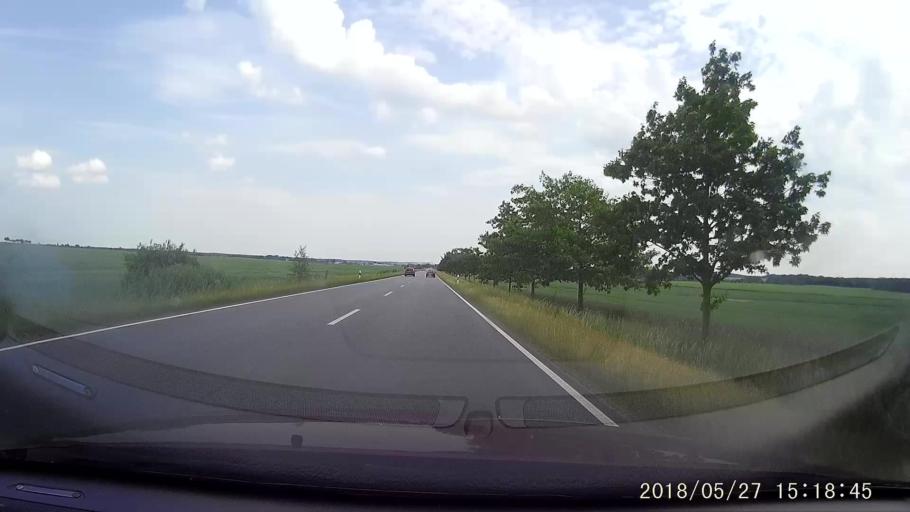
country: DE
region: Saxony
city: Kodersdorf
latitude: 51.2623
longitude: 14.8615
